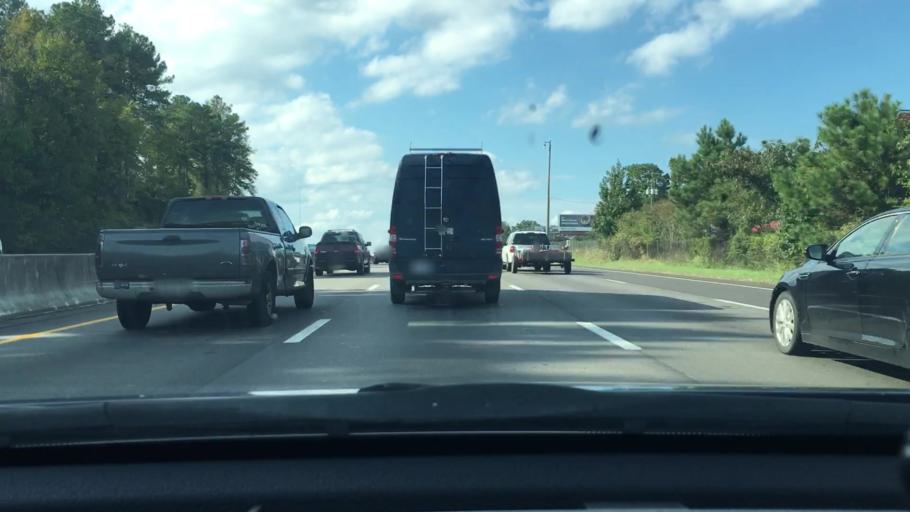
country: US
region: South Carolina
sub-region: Lexington County
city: Saint Andrews
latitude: 34.0463
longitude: -81.1196
